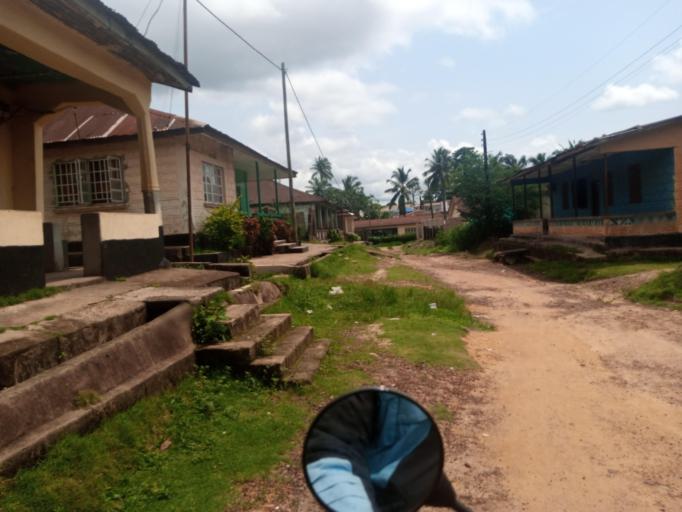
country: SL
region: Southern Province
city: Bo
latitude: 7.9572
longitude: -11.7389
